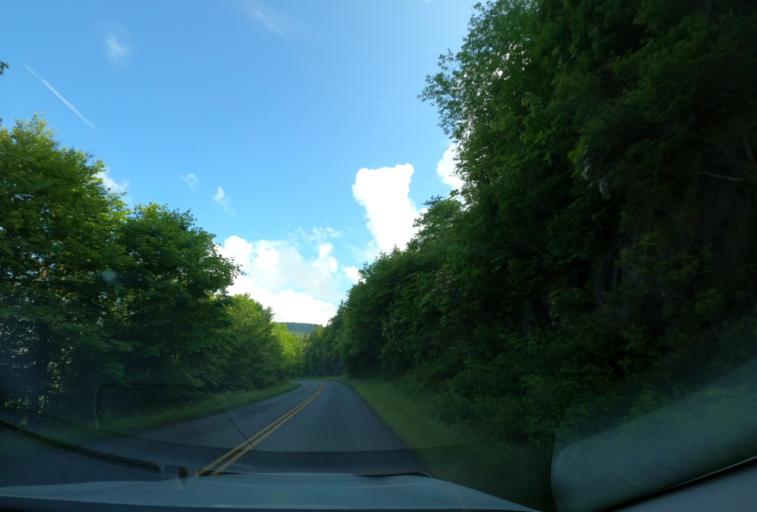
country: US
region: North Carolina
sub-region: Haywood County
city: Hazelwood
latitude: 35.3369
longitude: -82.9682
